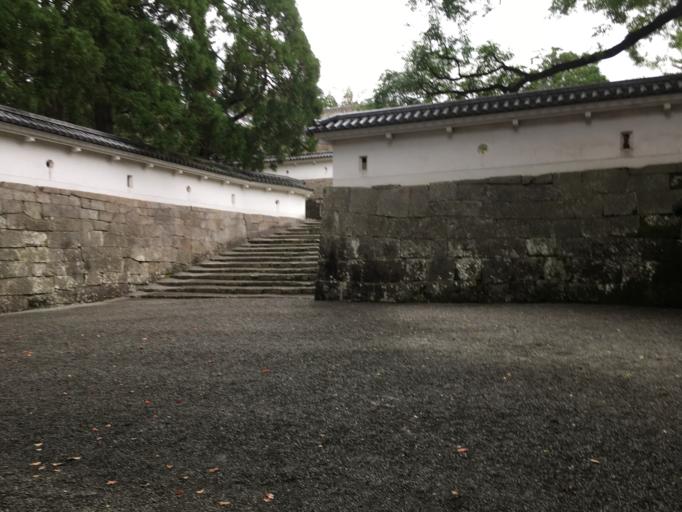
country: JP
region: Miyazaki
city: Nichinan
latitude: 31.6277
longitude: 131.3517
